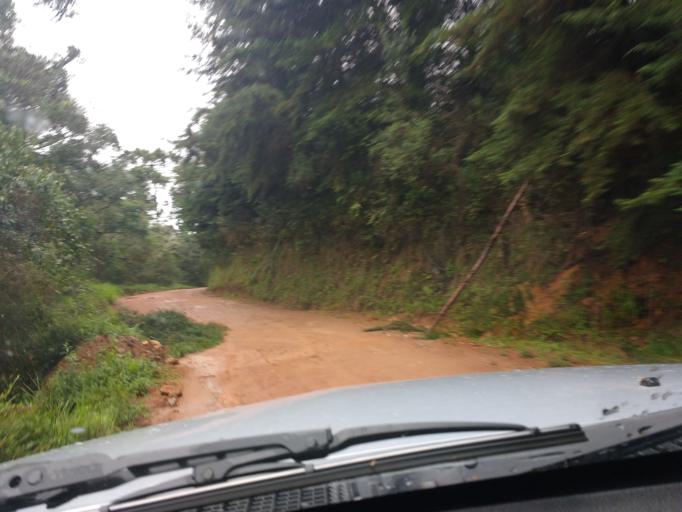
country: BR
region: Minas Gerais
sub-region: Cambui
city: Cambui
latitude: -22.7461
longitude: -45.9200
